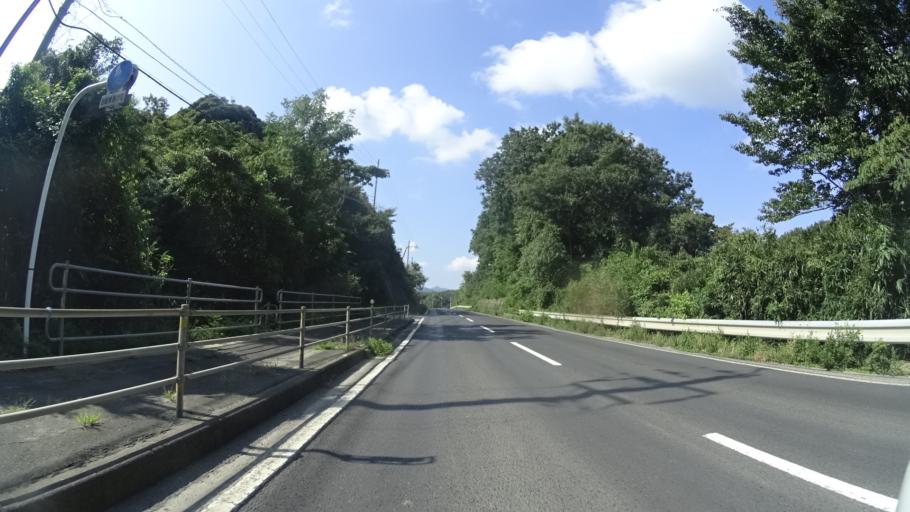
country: JP
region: Shimane
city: Gotsucho
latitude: 35.0484
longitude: 132.3068
